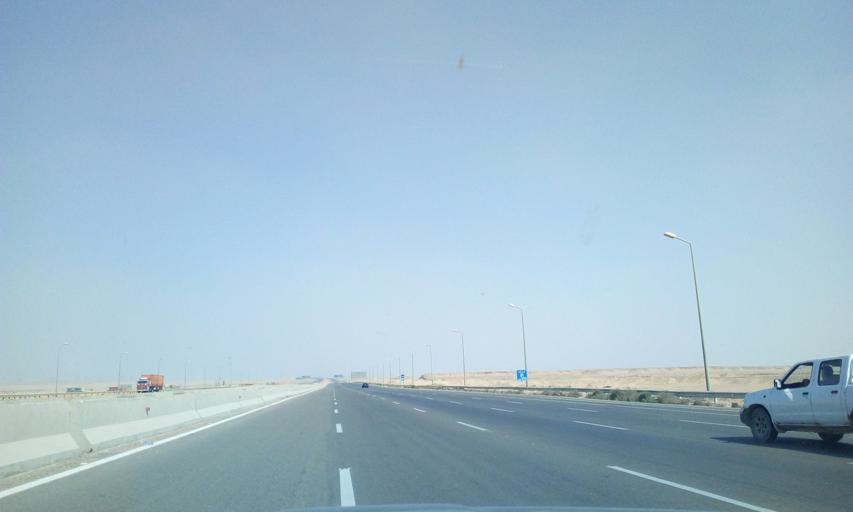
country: EG
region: Muhafazat al Qahirah
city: Halwan
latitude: 29.9038
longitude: 31.7557
